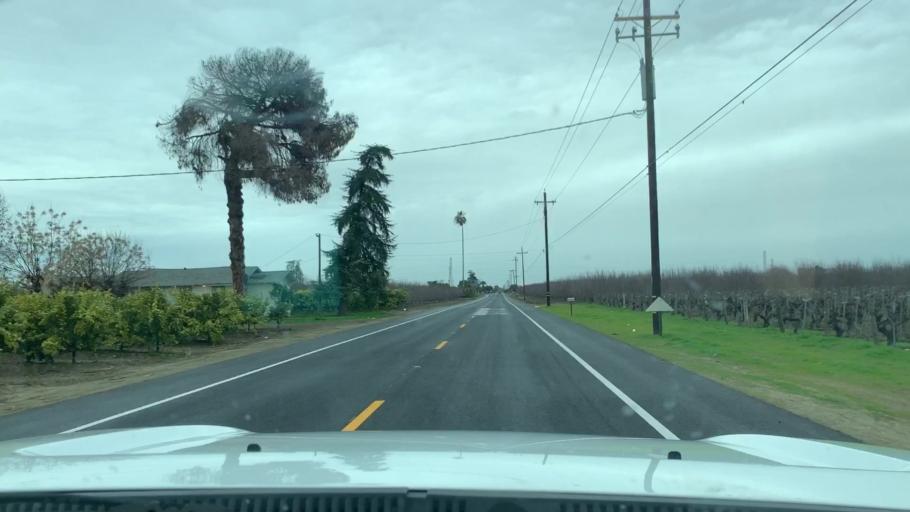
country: US
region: California
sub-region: Fresno County
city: Fowler
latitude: 36.5865
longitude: -119.6825
